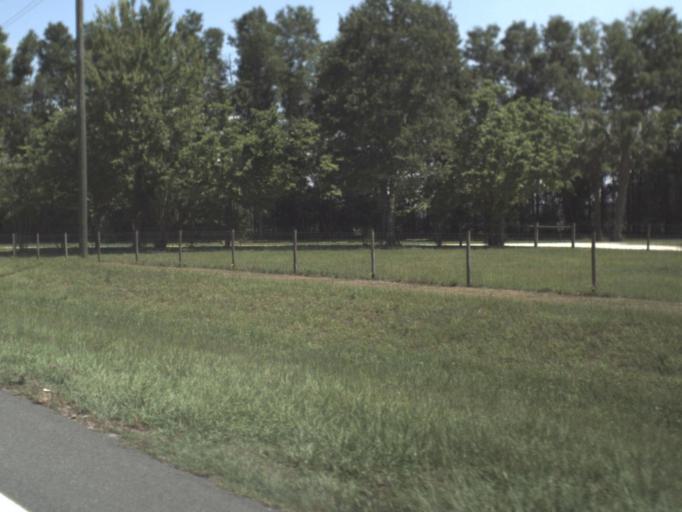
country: US
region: Florida
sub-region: Lafayette County
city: Mayo
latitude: 30.0672
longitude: -83.1977
